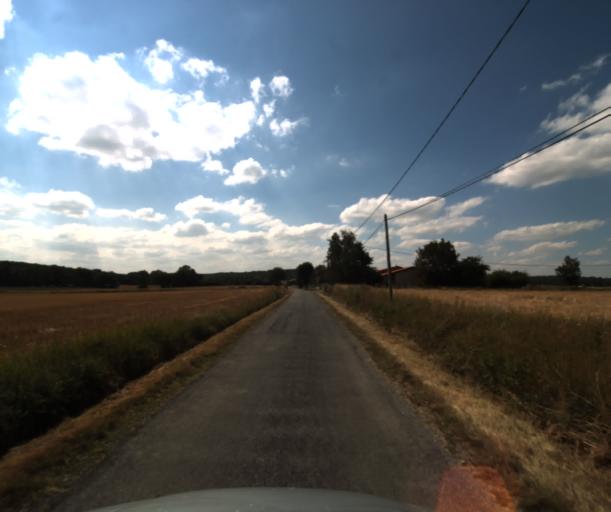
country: FR
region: Midi-Pyrenees
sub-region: Departement de la Haute-Garonne
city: Saint-Lys
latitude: 43.5266
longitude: 1.1653
